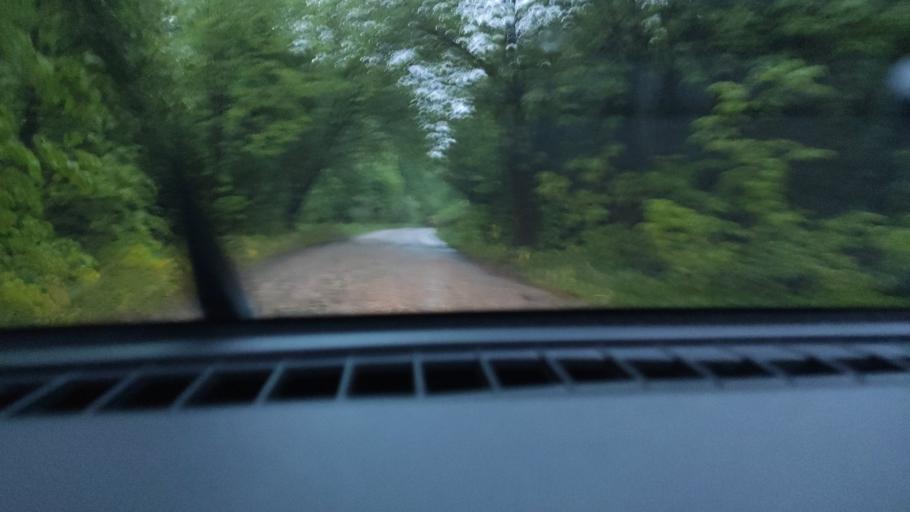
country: RU
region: Perm
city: Perm
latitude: 58.0976
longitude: 56.4126
